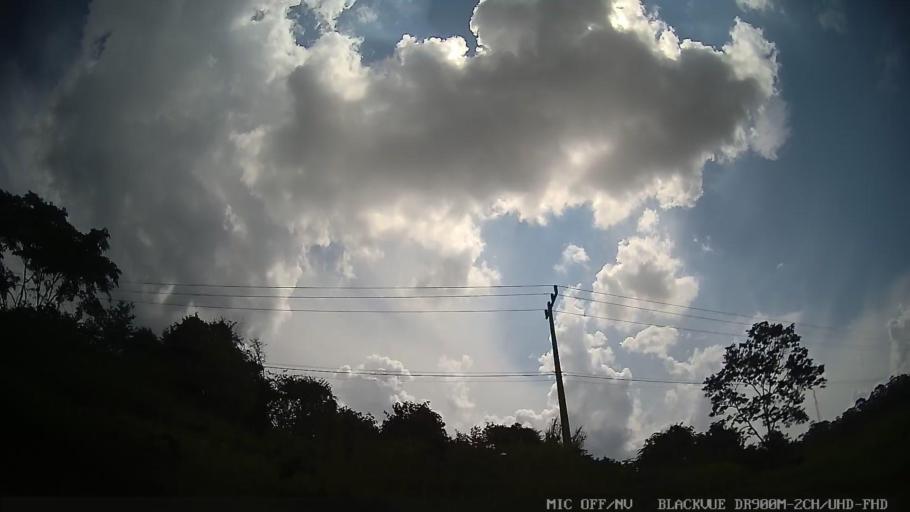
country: BR
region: Sao Paulo
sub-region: Braganca Paulista
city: Braganca Paulista
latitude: -22.9553
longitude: -46.5887
